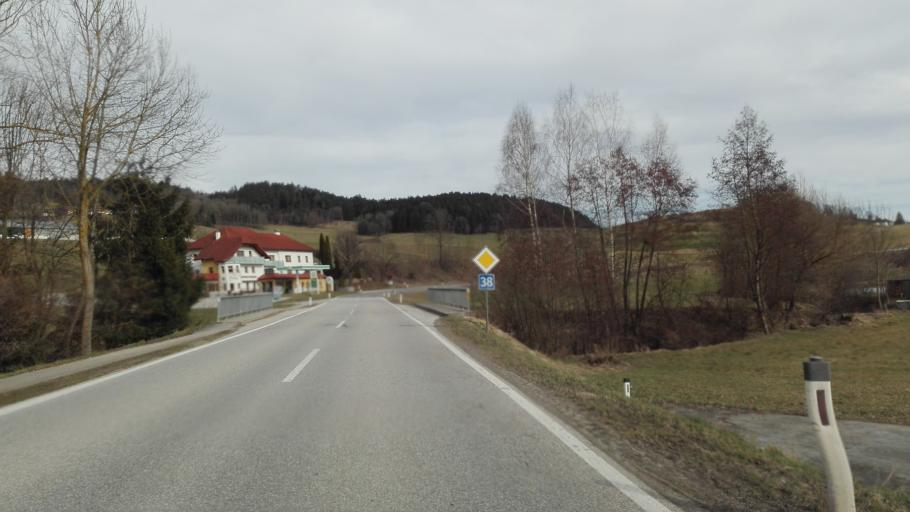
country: AT
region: Upper Austria
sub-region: Politischer Bezirk Rohrbach
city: Nebelberg
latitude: 48.6131
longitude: 13.9047
